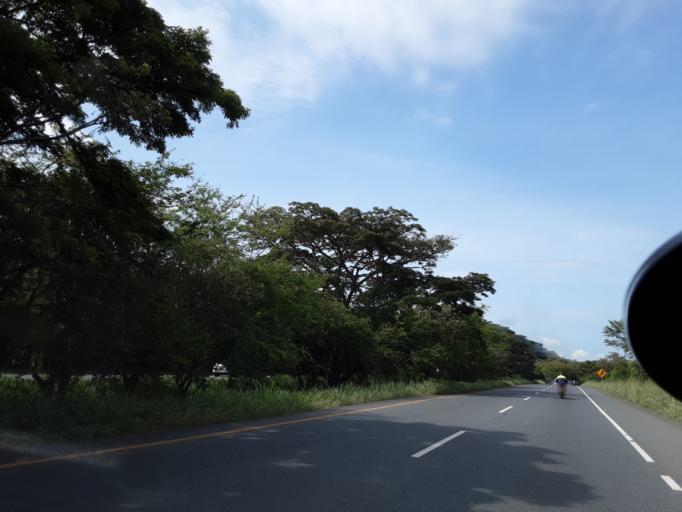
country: CO
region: Valle del Cauca
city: Buga
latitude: 3.8298
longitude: -76.3018
